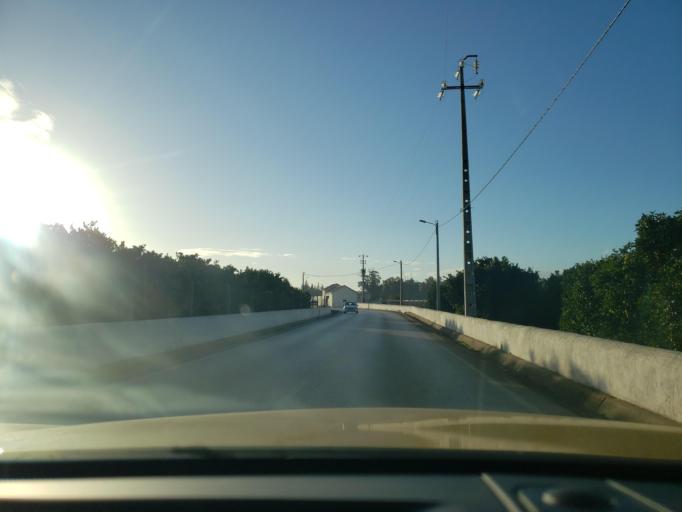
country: PT
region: Faro
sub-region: Portimao
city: Alvor
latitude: 37.1692
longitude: -8.5796
